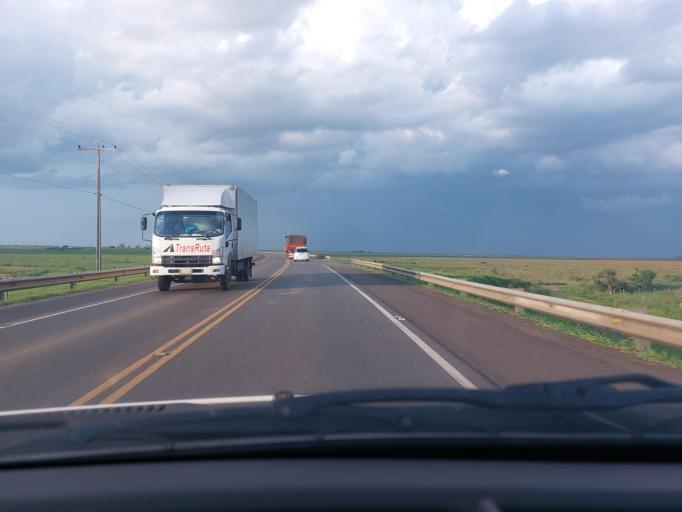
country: PY
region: Cordillera
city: Arroyos y Esteros
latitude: -25.0453
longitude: -57.0399
